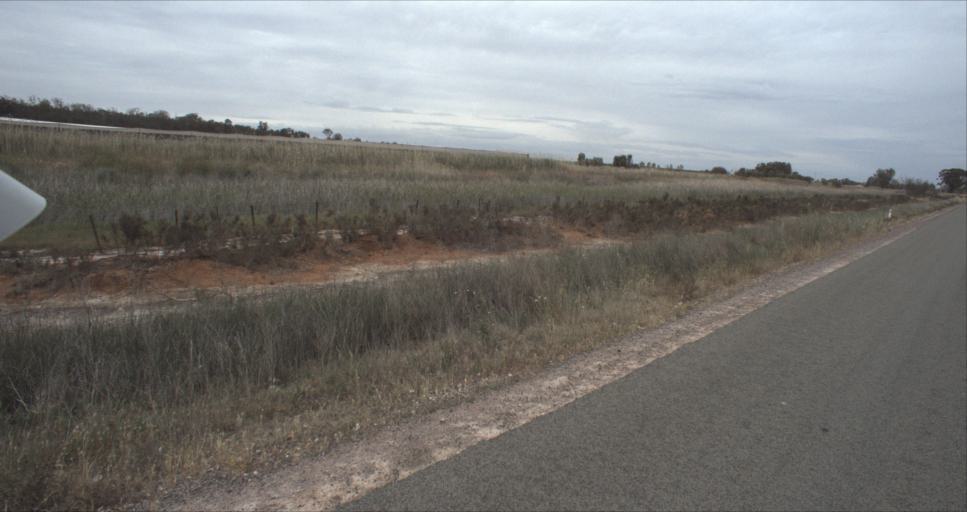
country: AU
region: New South Wales
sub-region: Leeton
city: Leeton
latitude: -34.4325
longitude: 146.3770
